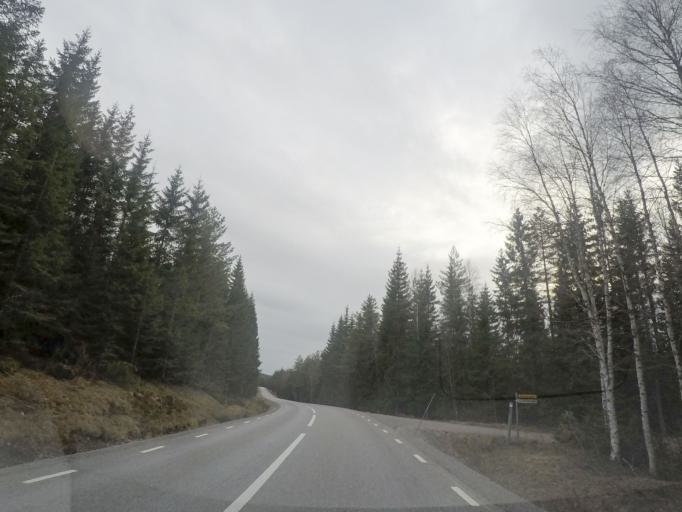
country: SE
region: OErebro
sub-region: Lindesbergs Kommun
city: Stora
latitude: 59.9007
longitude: 15.1943
